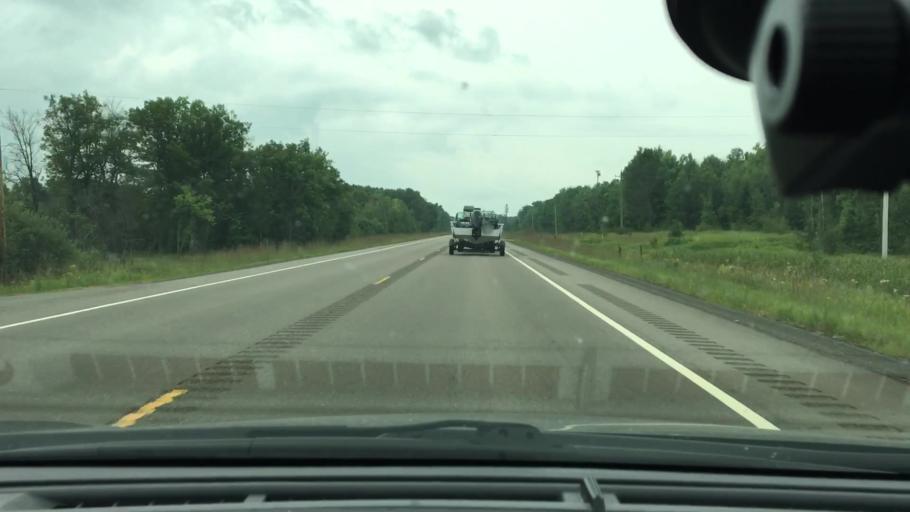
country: US
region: Minnesota
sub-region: Crow Wing County
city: Crosby
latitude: 46.5868
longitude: -93.9527
